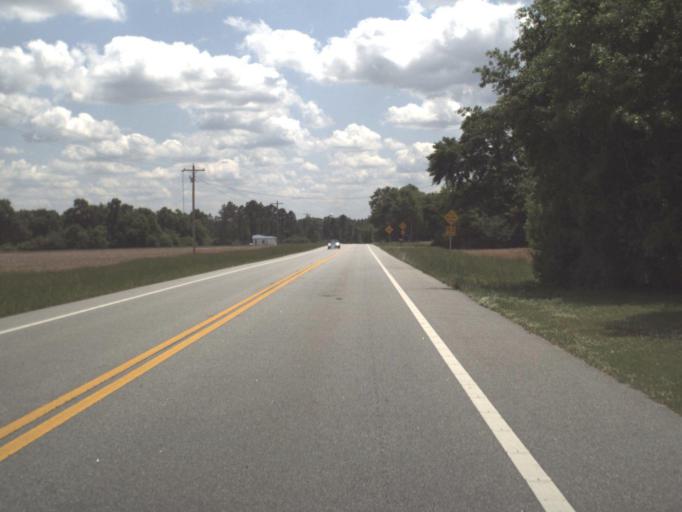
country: US
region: Alabama
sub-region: Escambia County
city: Atmore
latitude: 30.9144
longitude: -87.4795
